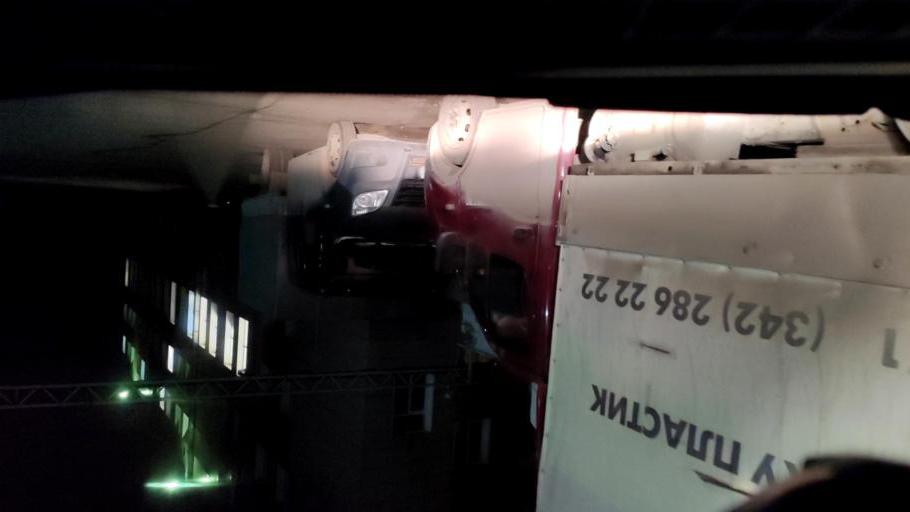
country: RU
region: Perm
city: Perm
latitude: 58.0123
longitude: 56.1908
